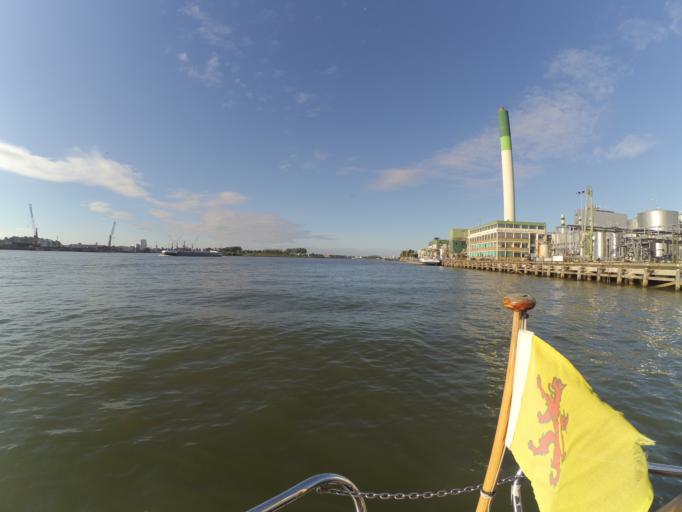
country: NL
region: South Holland
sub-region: Gemeente Zwijndrecht
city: Zwijndrecht
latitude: 51.8073
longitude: 4.6435
